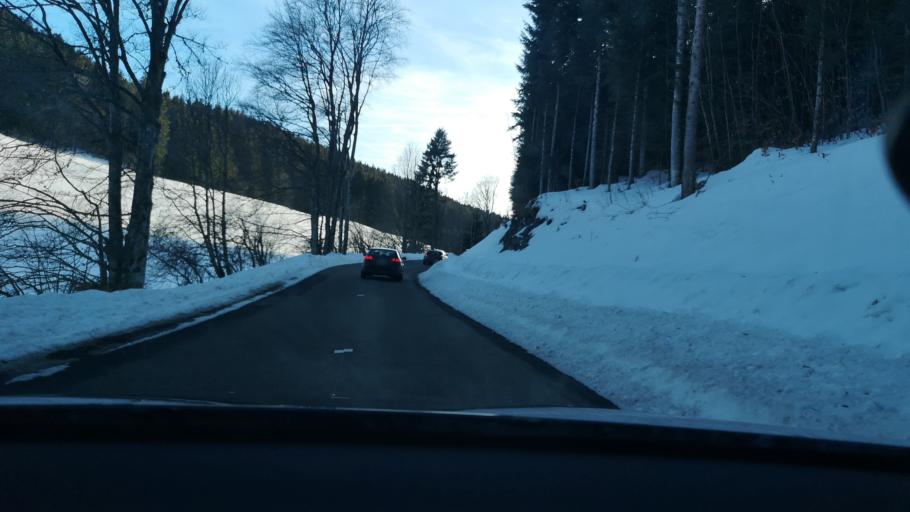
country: FR
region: Franche-Comte
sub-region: Departement du Doubs
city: Gilley
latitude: 46.9778
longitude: 6.4940
